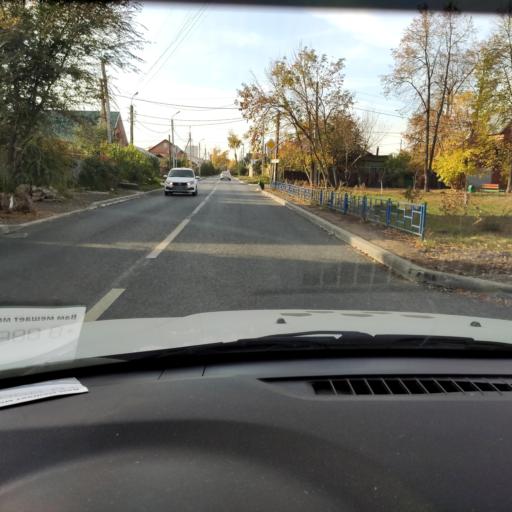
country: RU
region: Samara
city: Tol'yatti
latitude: 53.5302
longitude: 49.4185
